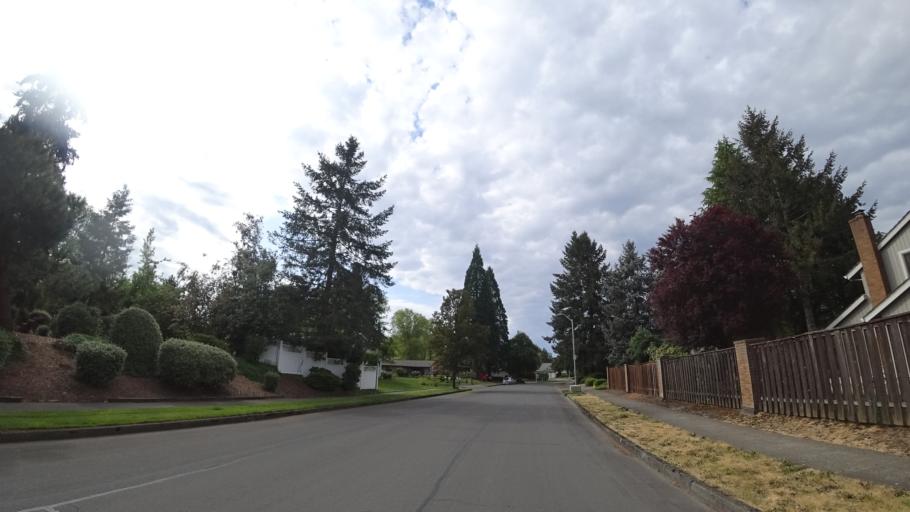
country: US
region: Oregon
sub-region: Washington County
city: Hillsboro
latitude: 45.4985
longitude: -122.9592
